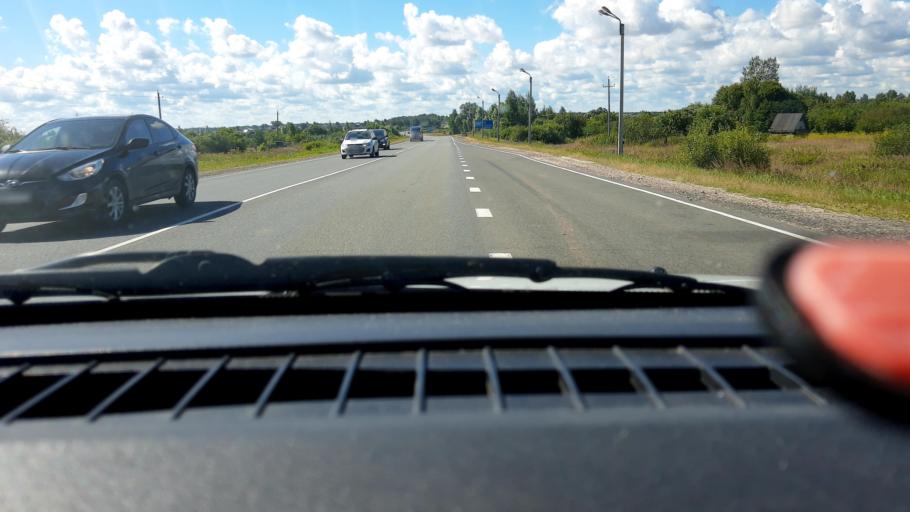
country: RU
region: Nizjnij Novgorod
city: Arzamas
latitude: 55.3410
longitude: 43.8905
